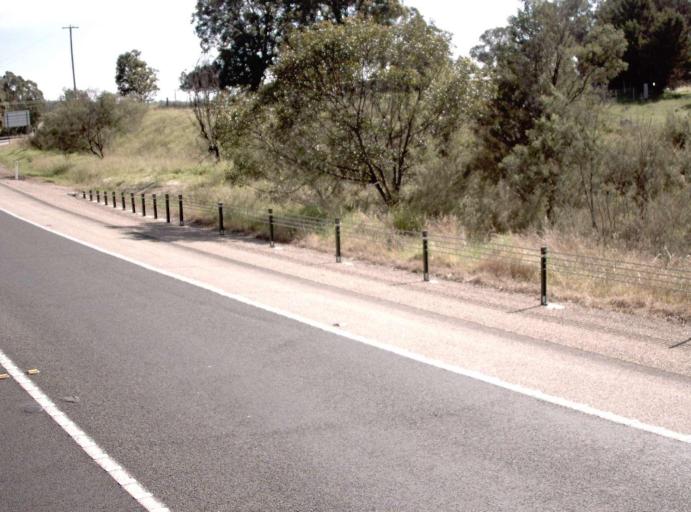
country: AU
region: Victoria
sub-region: East Gippsland
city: Bairnsdale
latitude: -37.7147
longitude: 147.8056
